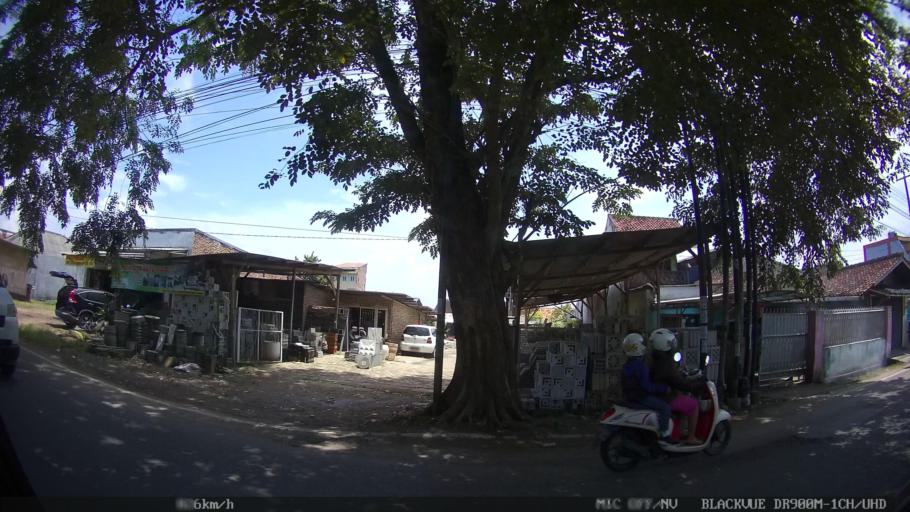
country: ID
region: Lampung
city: Kedaton
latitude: -5.3577
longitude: 105.2862
